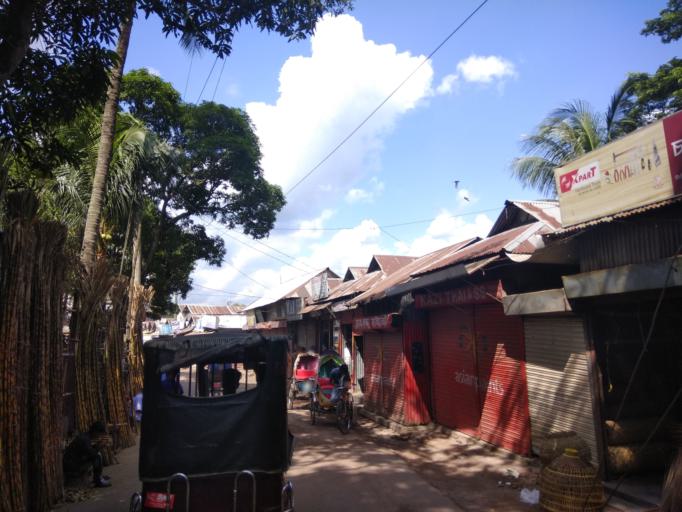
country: BD
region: Dhaka
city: Narayanganj
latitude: 23.5095
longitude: 90.4663
